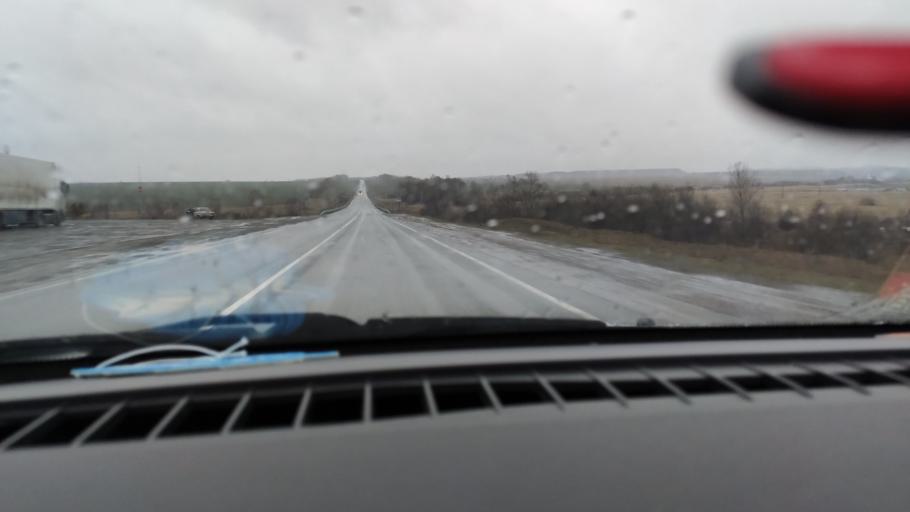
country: RU
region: Tatarstan
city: Mendeleyevsk
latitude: 55.9386
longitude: 52.2890
